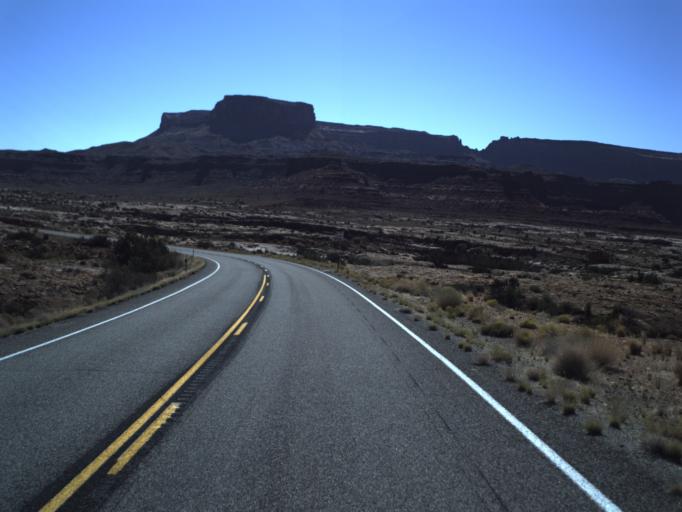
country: US
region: Utah
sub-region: San Juan County
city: Blanding
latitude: 37.8237
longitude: -110.3579
